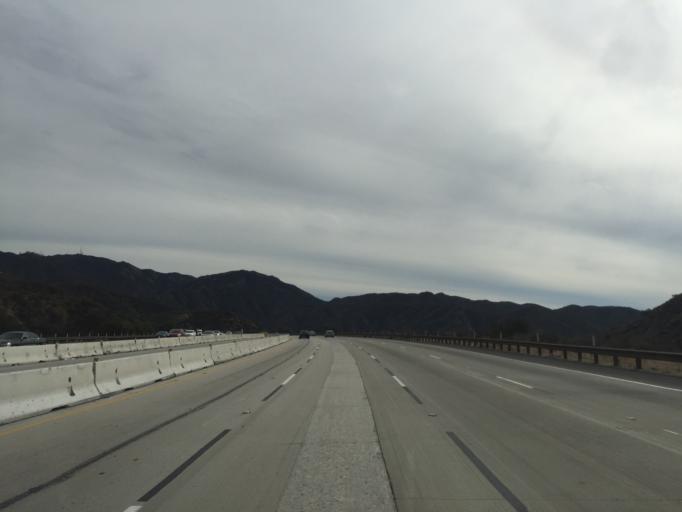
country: US
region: California
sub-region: Los Angeles County
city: Burbank
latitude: 34.2480
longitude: -118.3219
